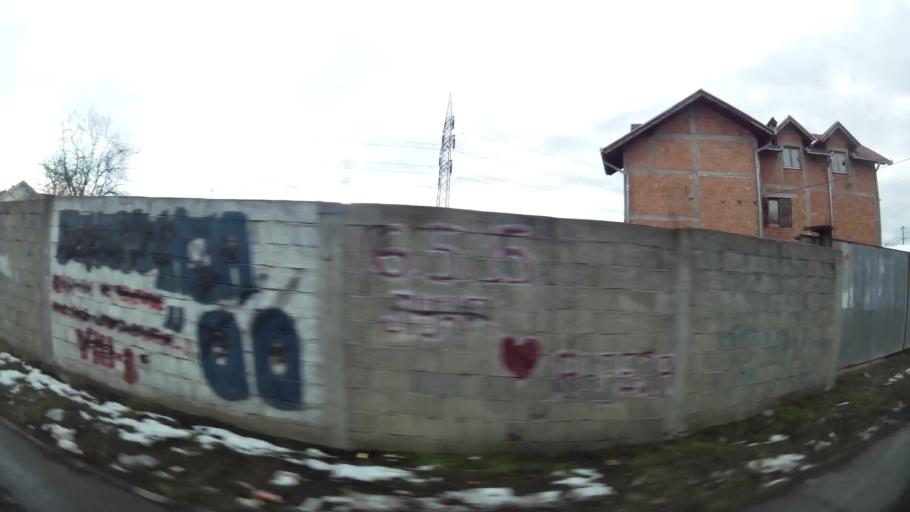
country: RS
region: Central Serbia
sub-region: Belgrade
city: Zvezdara
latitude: 44.7221
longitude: 20.5019
